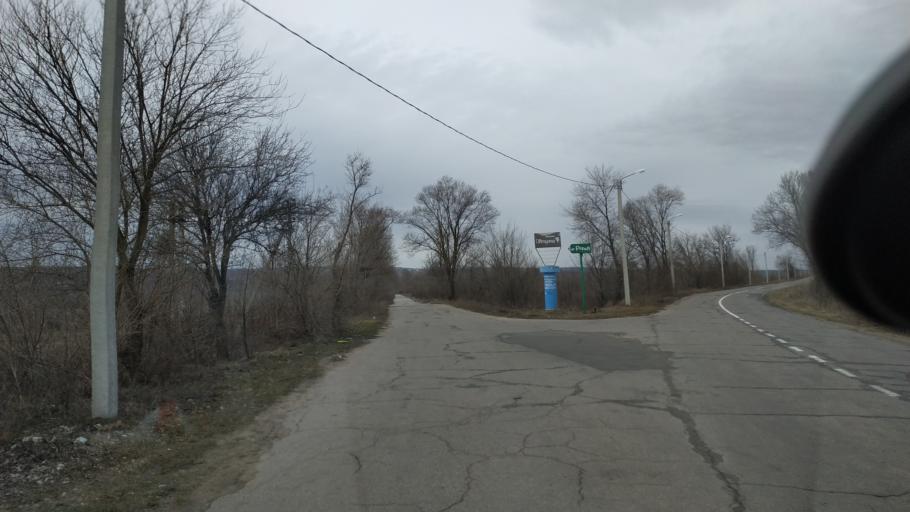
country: MD
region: Telenesti
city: Cocieri
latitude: 47.3245
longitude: 29.0974
